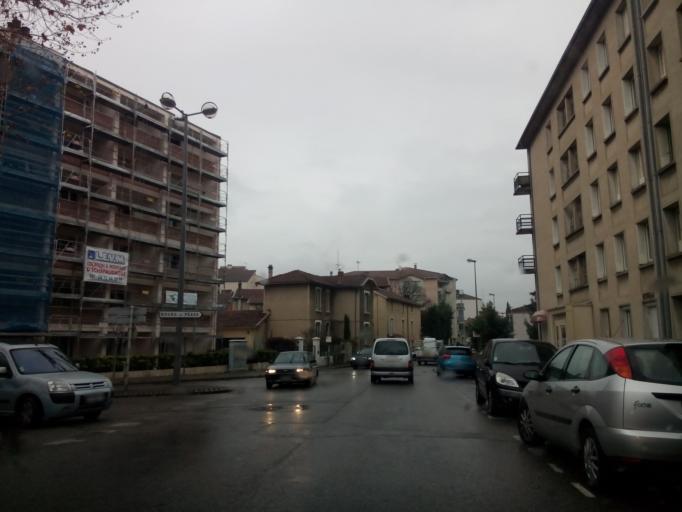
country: FR
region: Rhone-Alpes
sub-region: Departement de la Drome
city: Romans-sur-Isere
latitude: 45.0483
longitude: 5.0408
